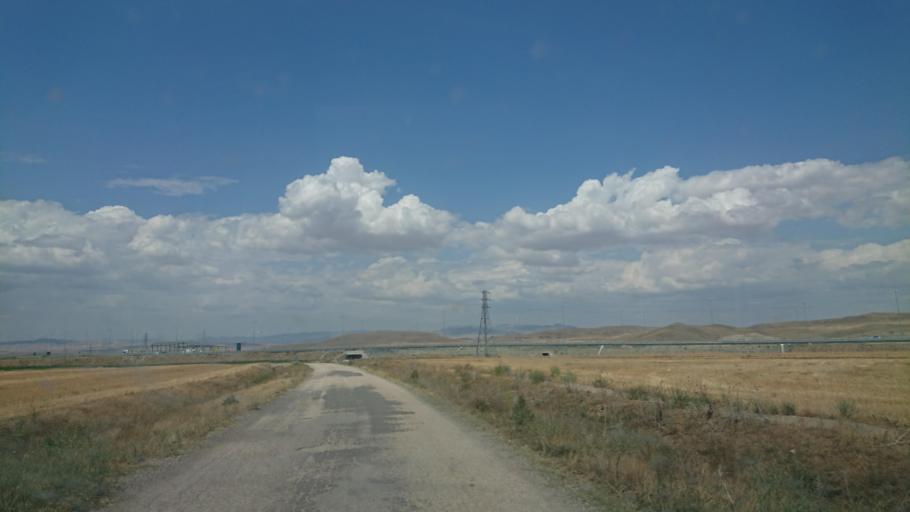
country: TR
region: Aksaray
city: Sariyahsi
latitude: 38.9718
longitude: 33.8988
